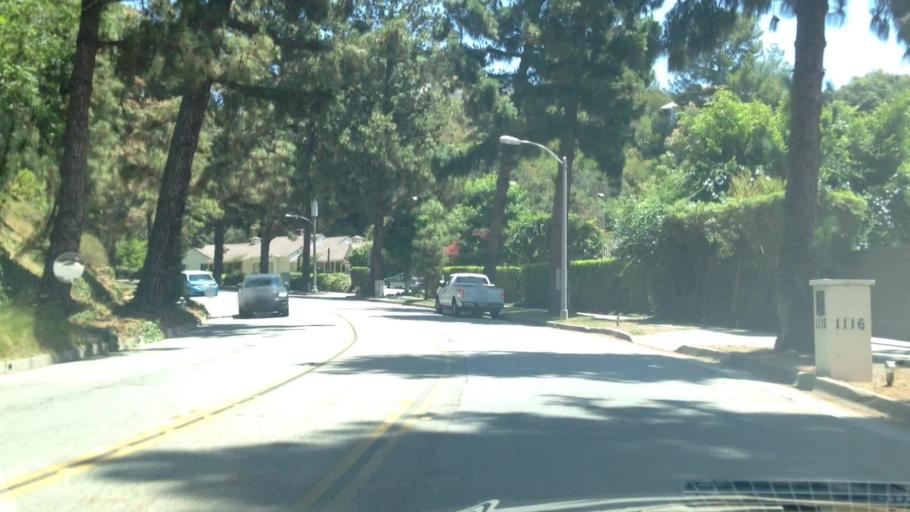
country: US
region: California
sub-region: Los Angeles County
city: Beverly Hills
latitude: 34.0922
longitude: -118.4092
